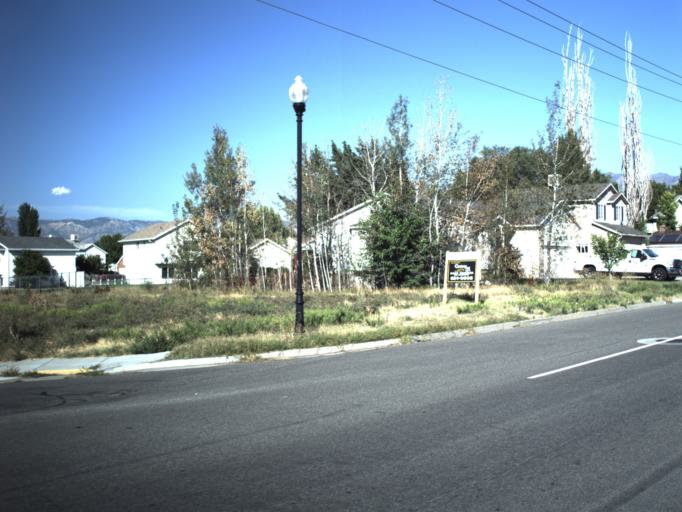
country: US
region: Utah
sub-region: Davis County
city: Clinton
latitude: 41.1399
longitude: -112.0416
